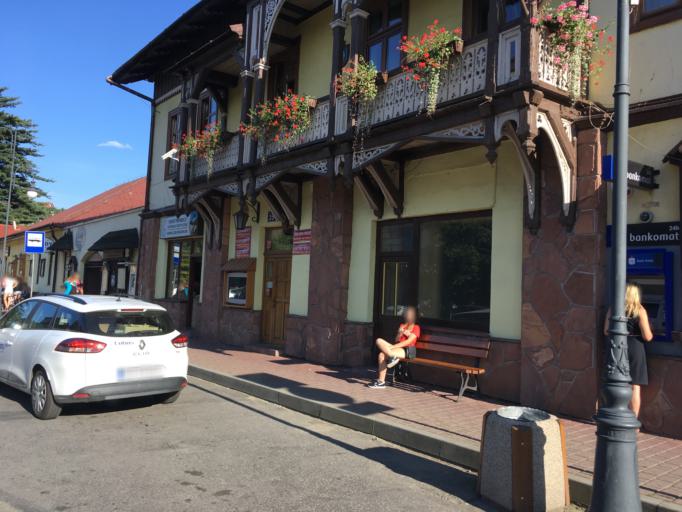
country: PL
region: Lesser Poland Voivodeship
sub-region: Powiat nowotarski
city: Kroscienko nad Dunajcem
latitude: 49.4406
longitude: 20.4281
